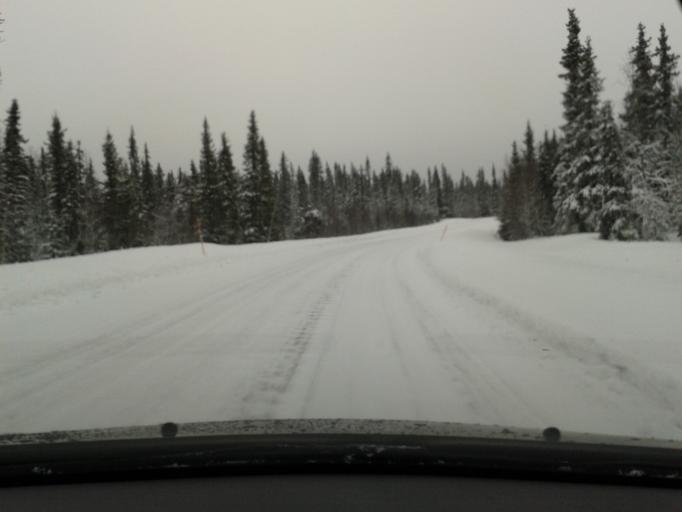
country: SE
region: Vaesterbotten
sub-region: Vilhelmina Kommun
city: Sjoberg
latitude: 65.1181
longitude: 15.8831
